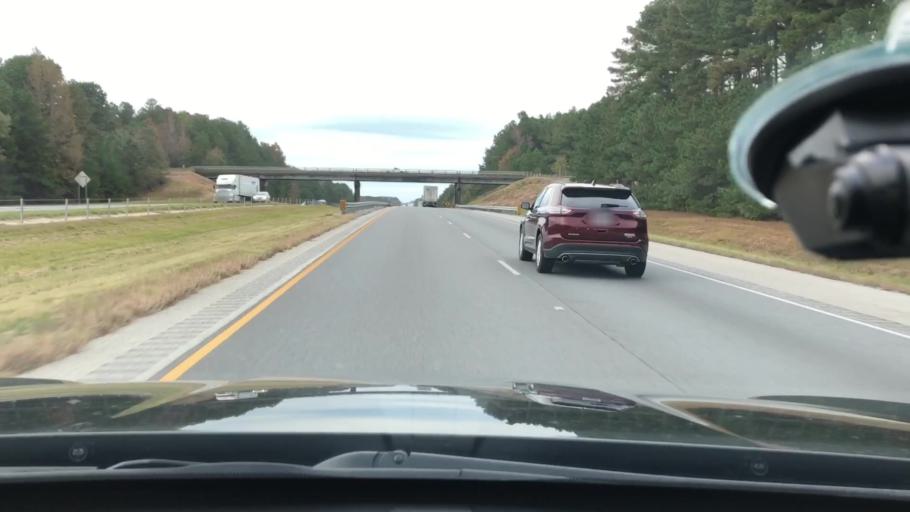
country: US
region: Arkansas
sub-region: Clark County
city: Arkadelphia
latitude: 34.0719
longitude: -93.1207
